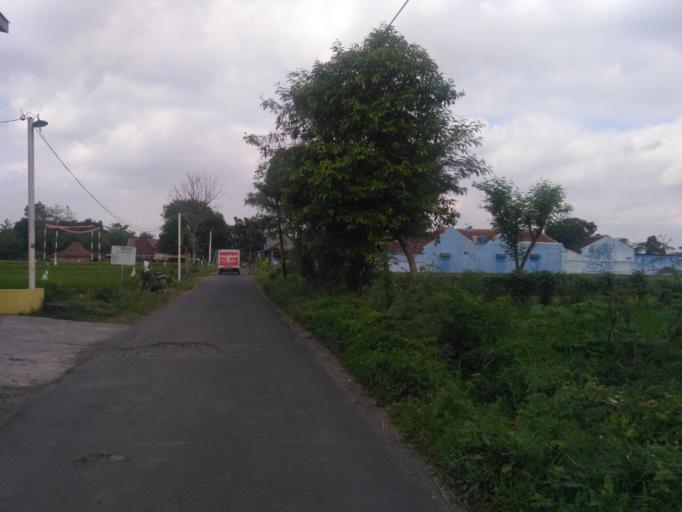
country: ID
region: Daerah Istimewa Yogyakarta
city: Melati
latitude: -7.7502
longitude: 110.3557
